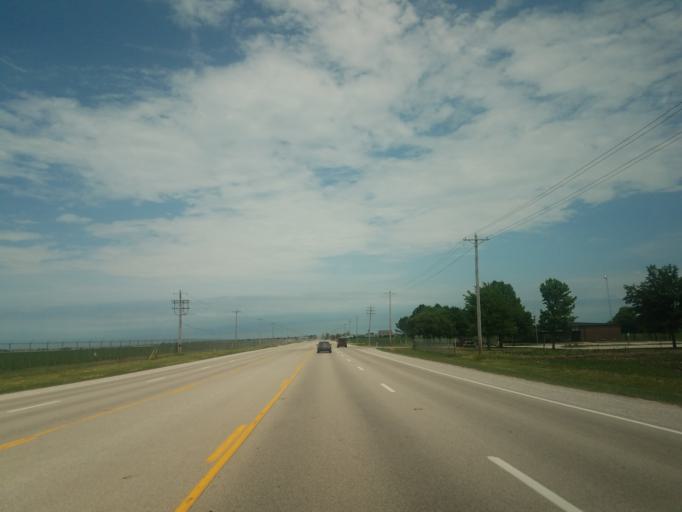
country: US
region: Illinois
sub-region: McLean County
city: Downs
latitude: 40.4775
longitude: -88.9023
